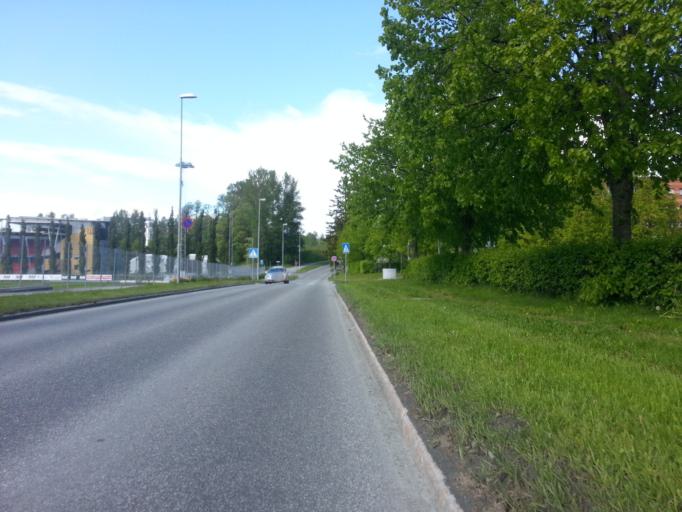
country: NO
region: Sor-Trondelag
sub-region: Trondheim
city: Trondheim
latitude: 63.4104
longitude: 10.4071
